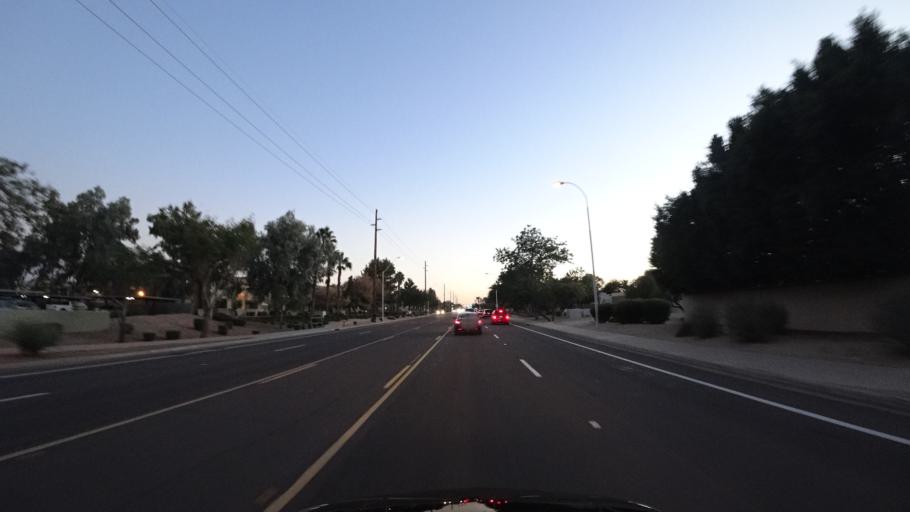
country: US
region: Arizona
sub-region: Maricopa County
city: Chandler
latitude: 33.3165
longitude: -111.8764
